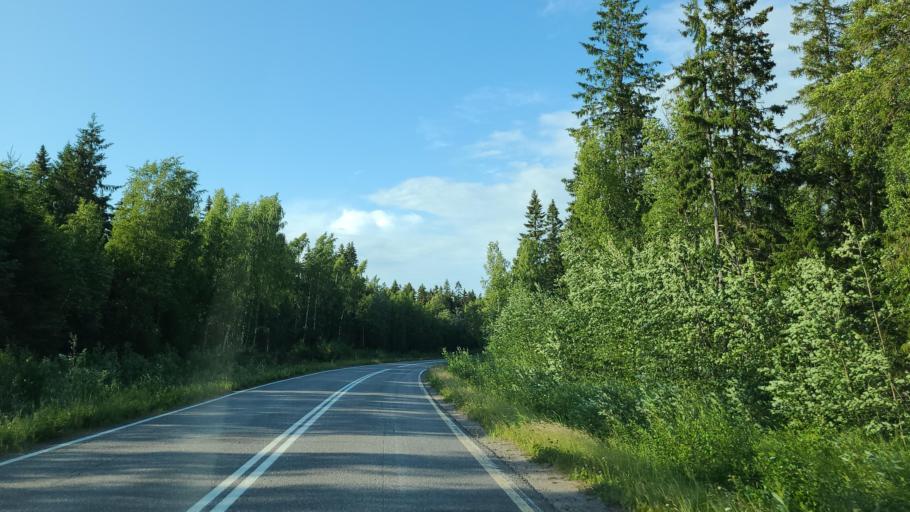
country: FI
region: Ostrobothnia
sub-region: Vaasa
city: Replot
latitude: 63.2938
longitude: 21.3551
